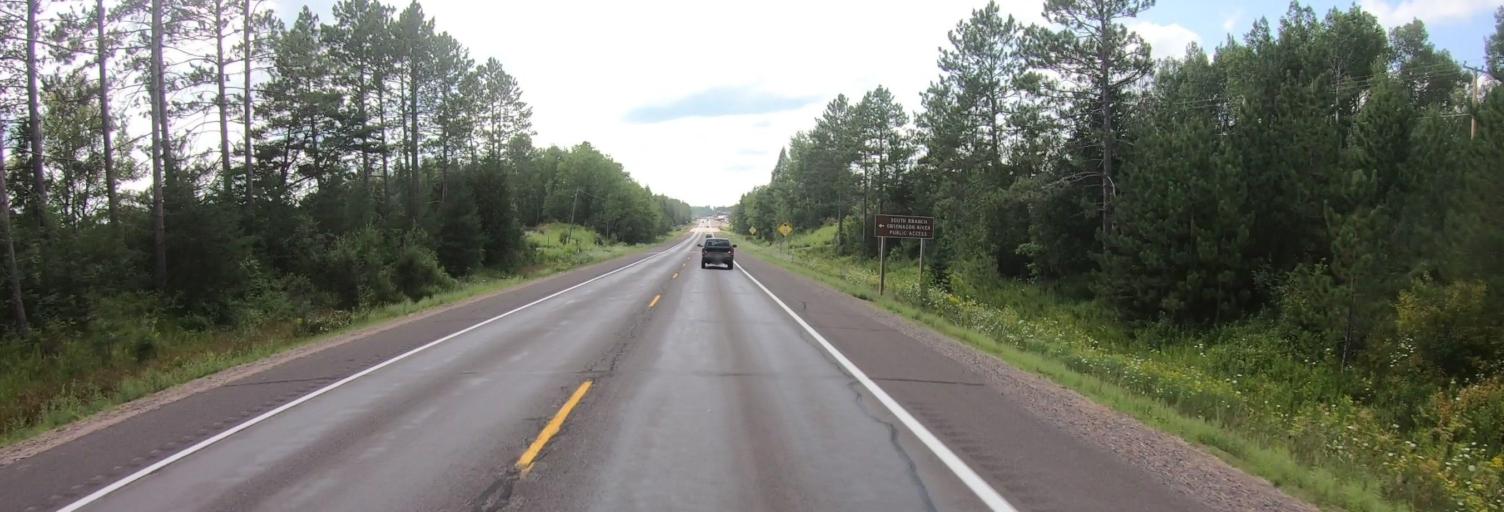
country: US
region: Michigan
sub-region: Ontonagon County
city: Ontonagon
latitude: 46.5348
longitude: -89.2711
